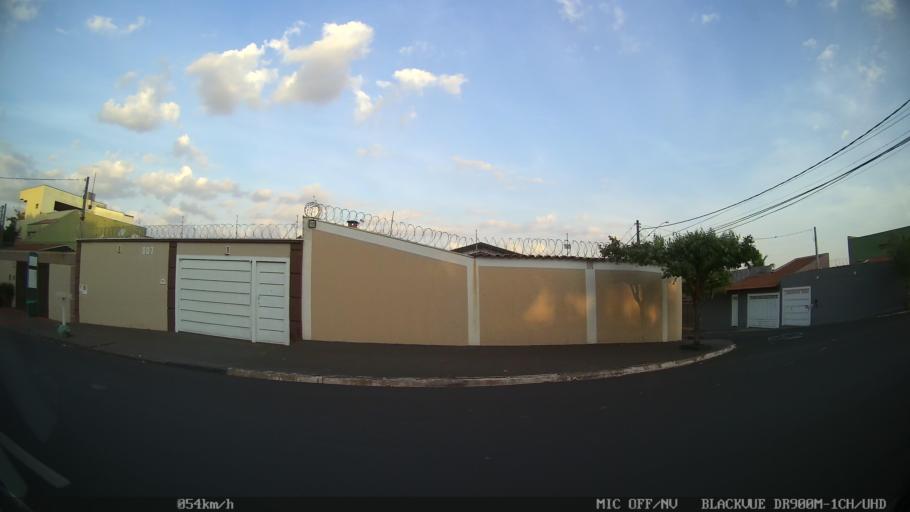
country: BR
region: Sao Paulo
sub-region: Ribeirao Preto
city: Ribeirao Preto
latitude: -21.1363
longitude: -47.8476
